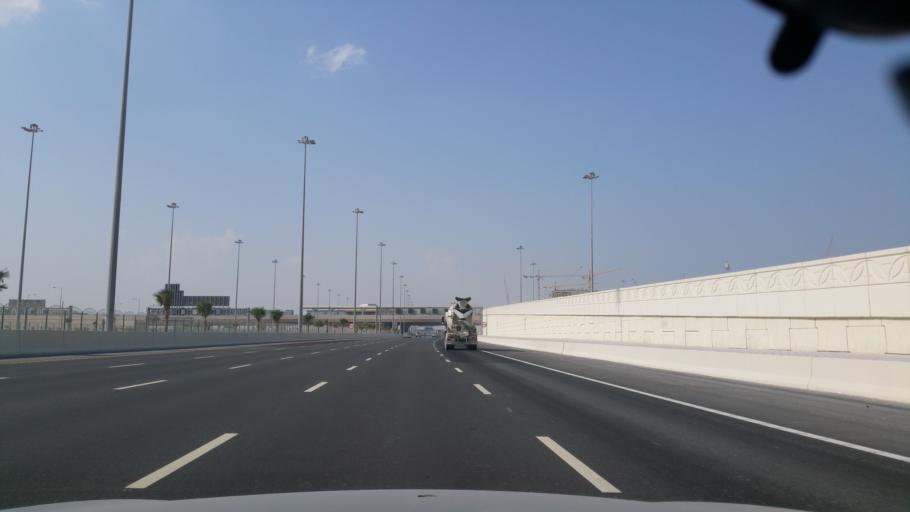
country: QA
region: Baladiyat Umm Salal
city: Umm Salal Muhammad
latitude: 25.4099
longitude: 51.4893
